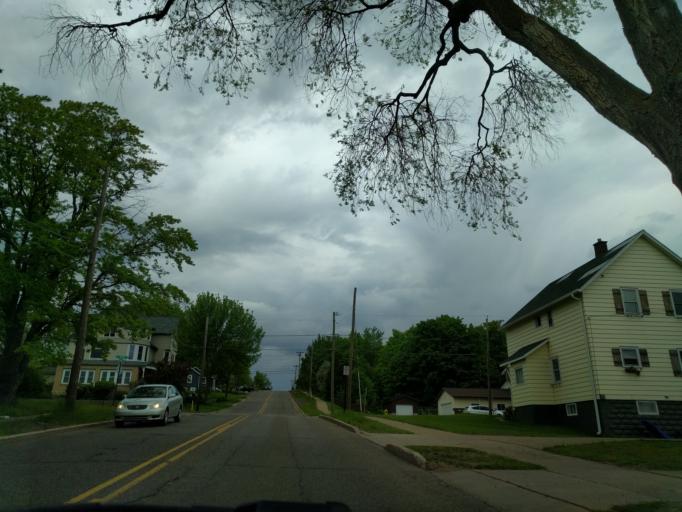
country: US
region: Michigan
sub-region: Marquette County
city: Marquette
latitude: 46.5464
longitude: -87.4124
